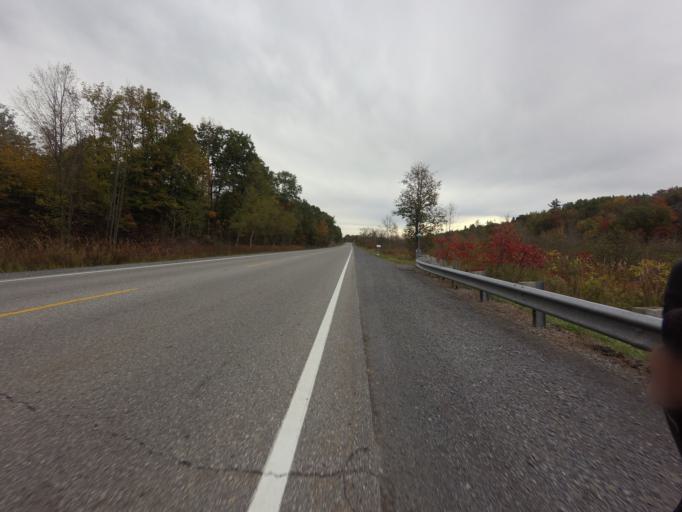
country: CA
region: Ontario
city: Gananoque
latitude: 44.3951
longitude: -76.3178
